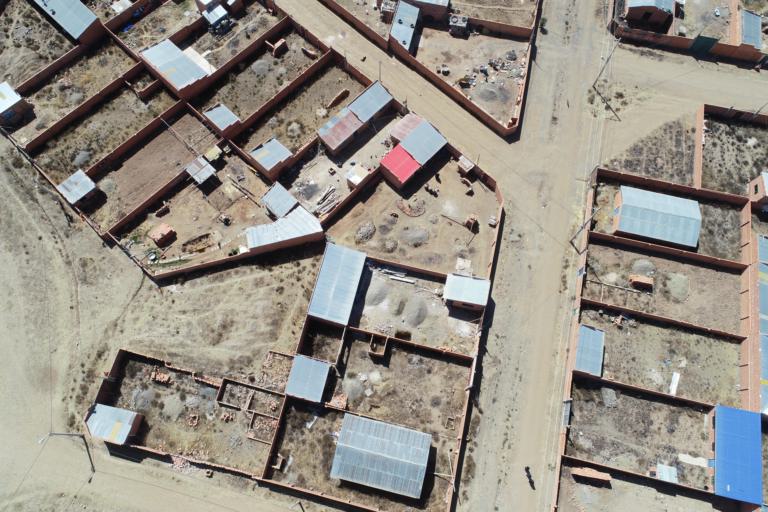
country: BO
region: La Paz
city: La Paz
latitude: -16.5930
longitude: -68.2126
